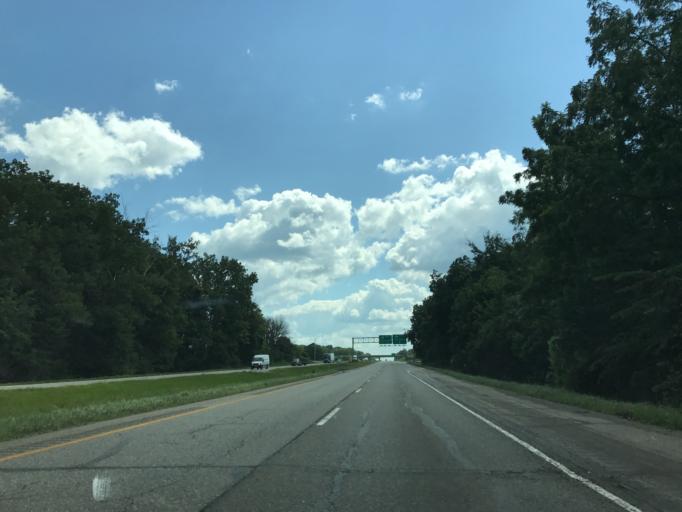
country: US
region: Indiana
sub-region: Marshall County
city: Plymouth
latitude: 41.3541
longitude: -86.2803
